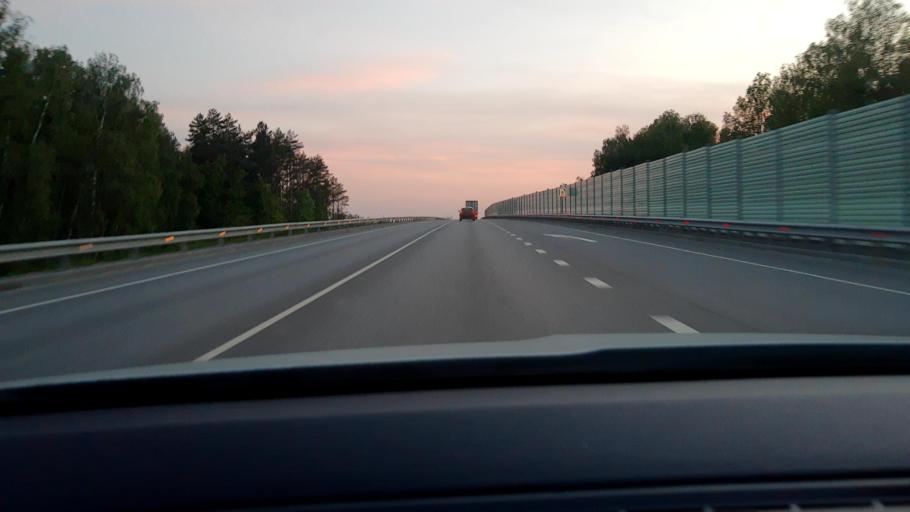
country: RU
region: Moskovskaya
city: Proletarskiy
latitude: 55.0304
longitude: 37.4785
